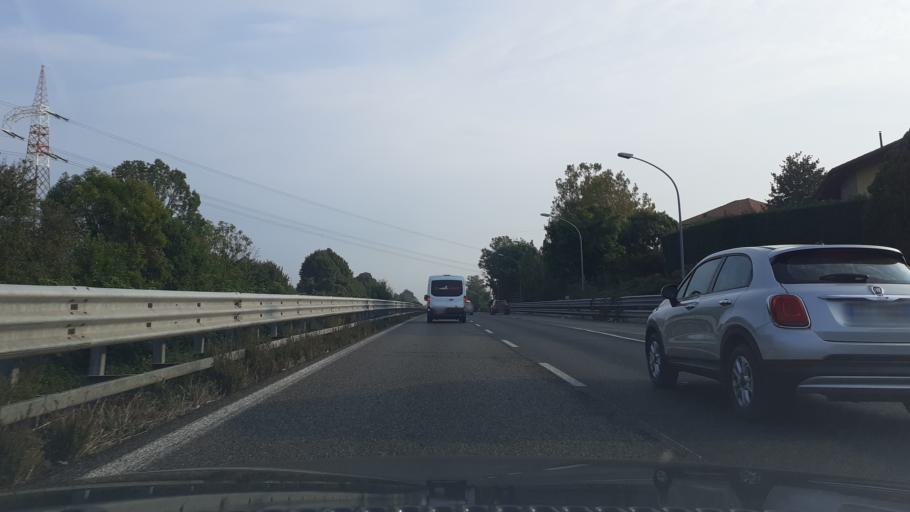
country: IT
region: Lombardy
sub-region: Provincia di Monza e Brianza
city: Verano Brianza
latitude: 45.6970
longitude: 9.2273
